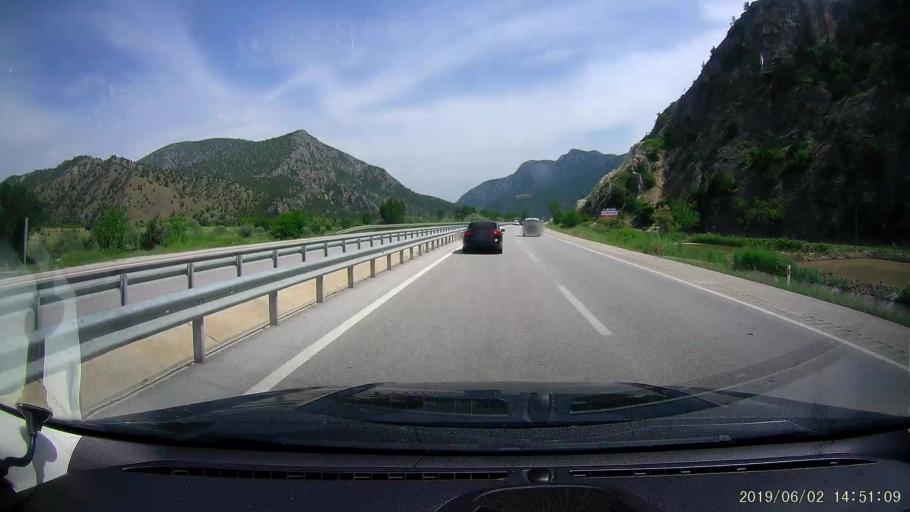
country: TR
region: Corum
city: Kargi
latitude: 41.0648
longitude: 34.5359
